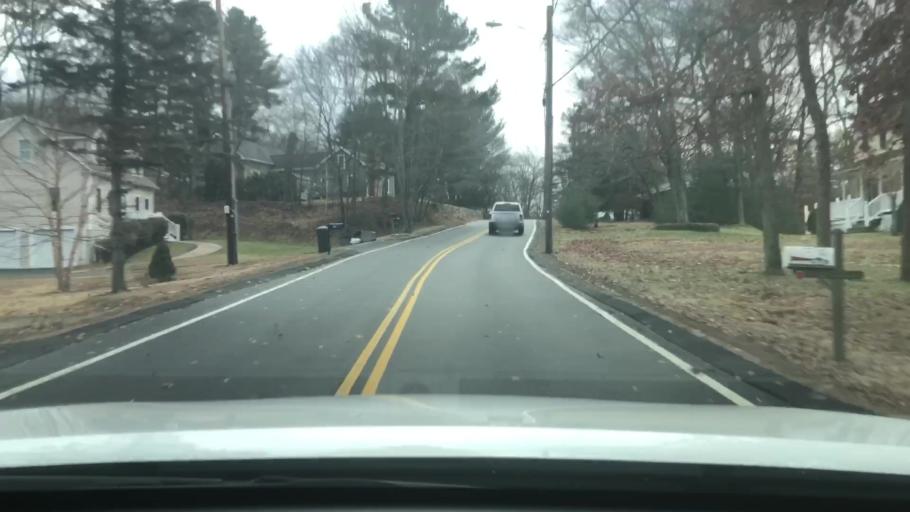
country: US
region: Massachusetts
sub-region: Worcester County
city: Blackstone
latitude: 42.0366
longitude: -71.5199
